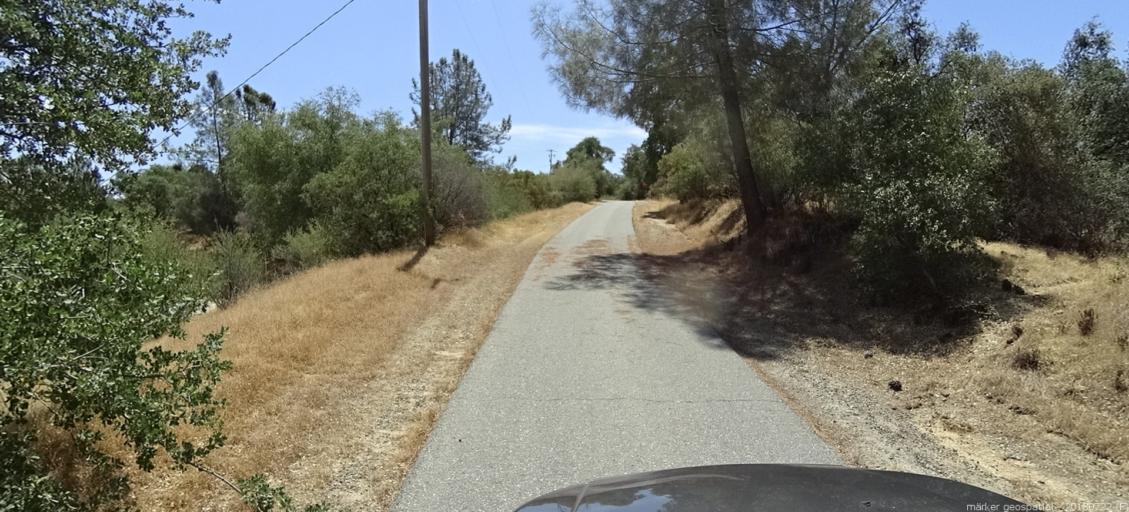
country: US
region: California
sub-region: Madera County
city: Coarsegold
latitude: 37.2807
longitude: -119.7602
